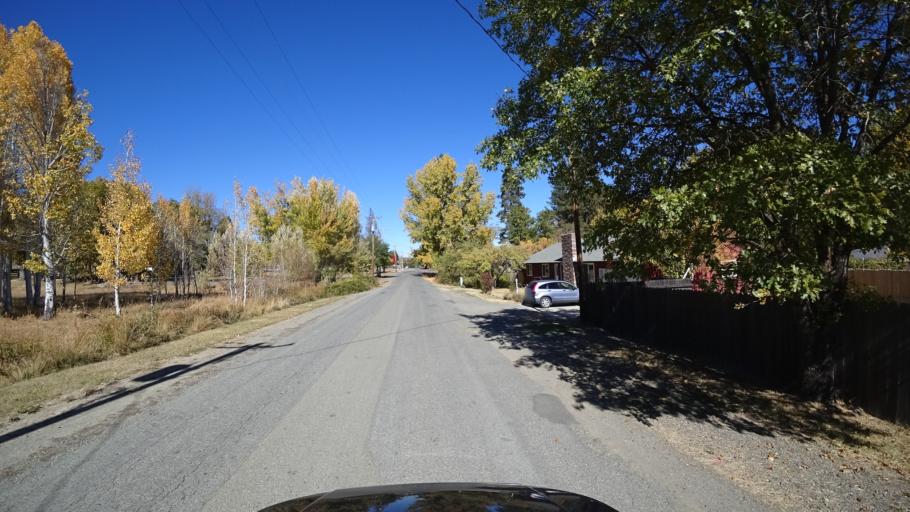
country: US
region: California
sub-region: Siskiyou County
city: Yreka
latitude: 41.4583
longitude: -122.8986
